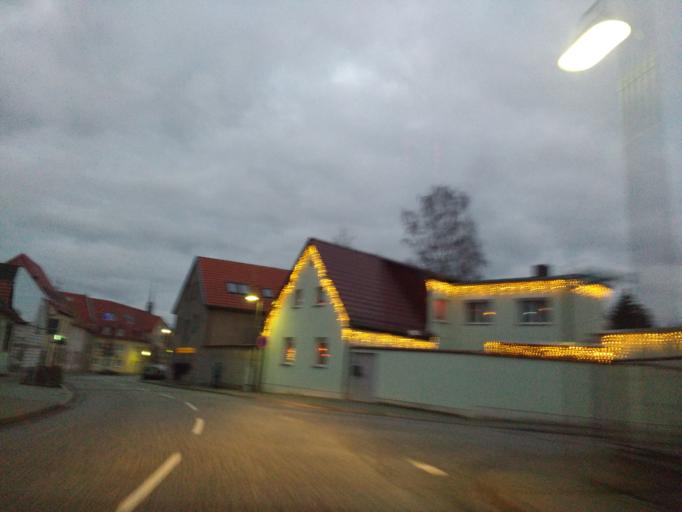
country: DE
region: Saxony-Anhalt
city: Bad Lauchstadt
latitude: 51.3847
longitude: 11.8647
